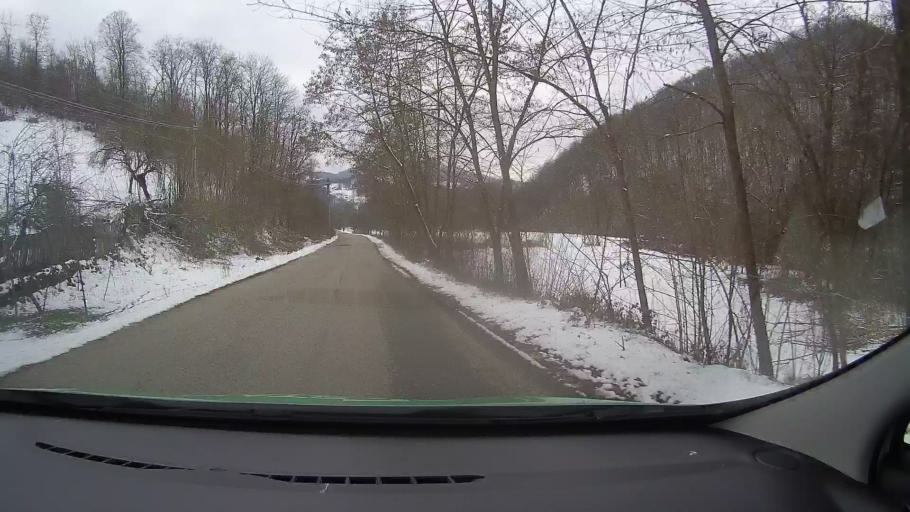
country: RO
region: Hunedoara
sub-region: Comuna Balsa
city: Balsa
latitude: 46.0523
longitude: 23.0712
